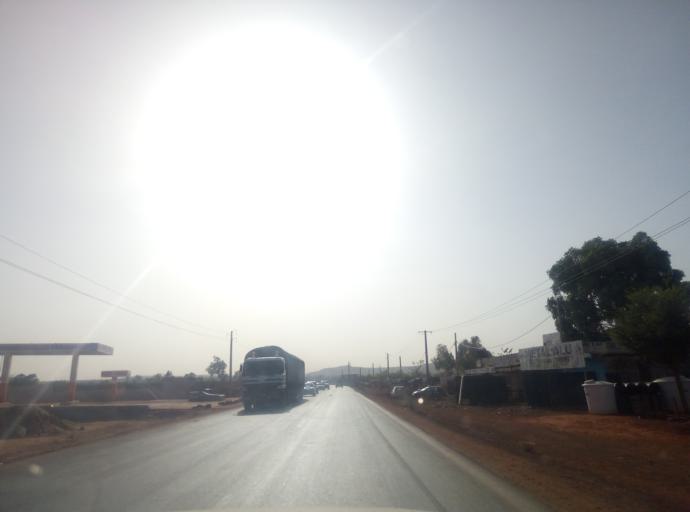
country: ML
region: Bamako
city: Bamako
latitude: 12.5863
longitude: -7.8293
